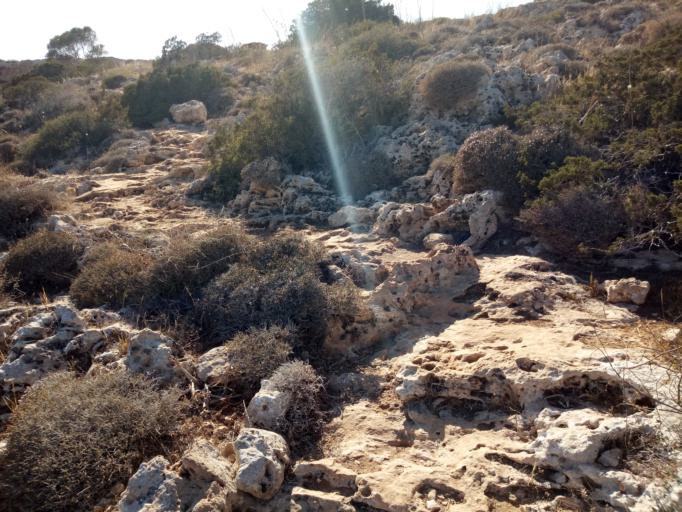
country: CY
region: Ammochostos
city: Protaras
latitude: 34.9680
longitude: 34.0716
